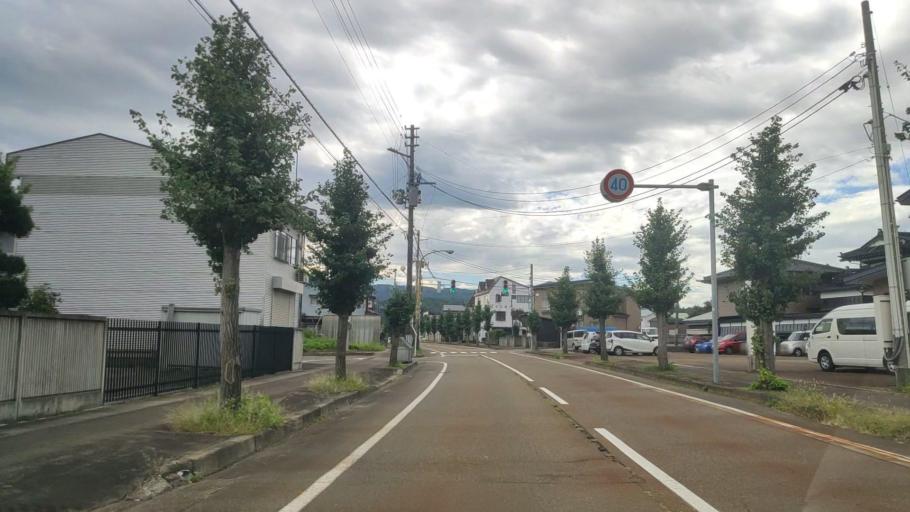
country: JP
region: Niigata
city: Arai
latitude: 37.0218
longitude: 138.2465
